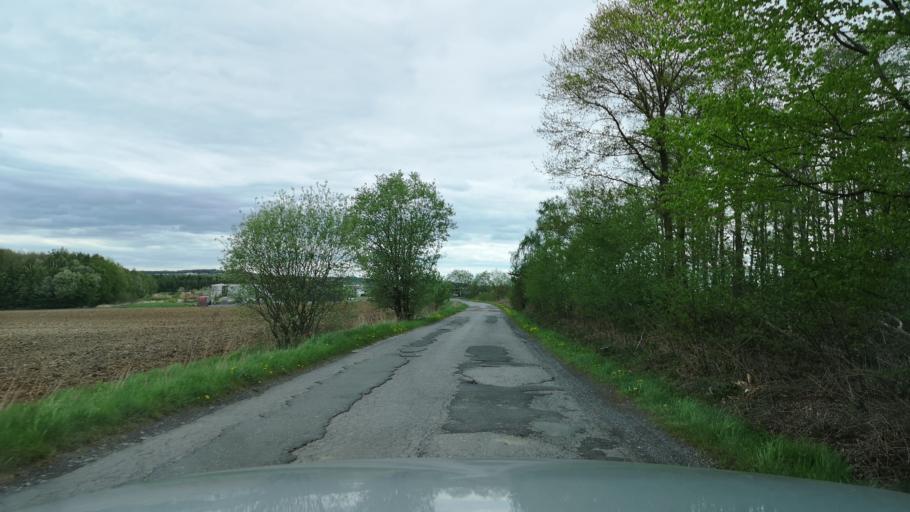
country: DE
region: North Rhine-Westphalia
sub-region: Regierungsbezirk Arnsberg
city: Menden
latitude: 51.4442
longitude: 7.7363
